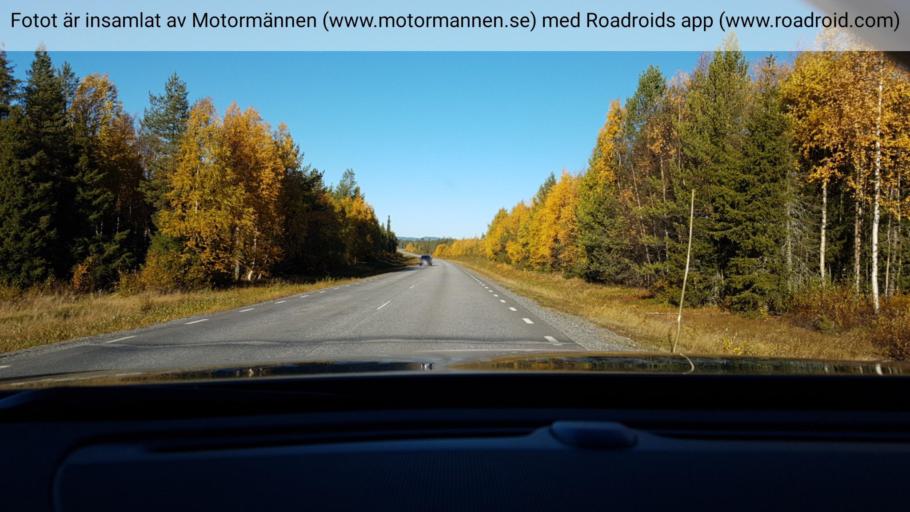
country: SE
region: Vaesterbotten
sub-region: Skelleftea Kommun
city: Storvik
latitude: 65.3712
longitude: 20.3918
